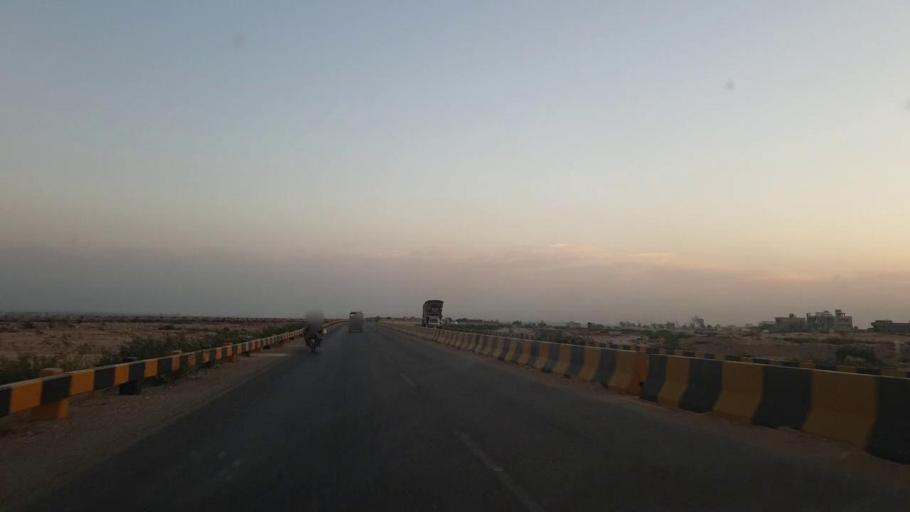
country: PK
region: Sindh
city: Jamshoro
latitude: 25.3963
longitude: 68.2738
